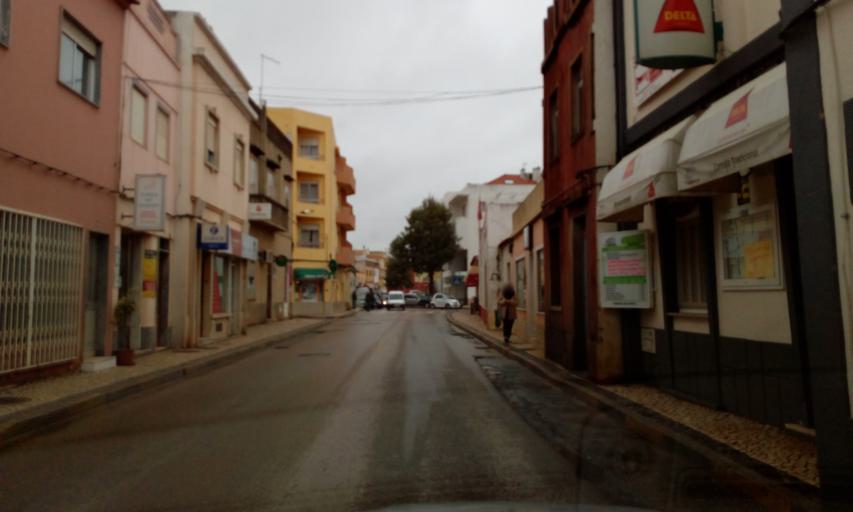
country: PT
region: Faro
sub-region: Albufeira
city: Guia
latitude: 37.1639
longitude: -8.3034
